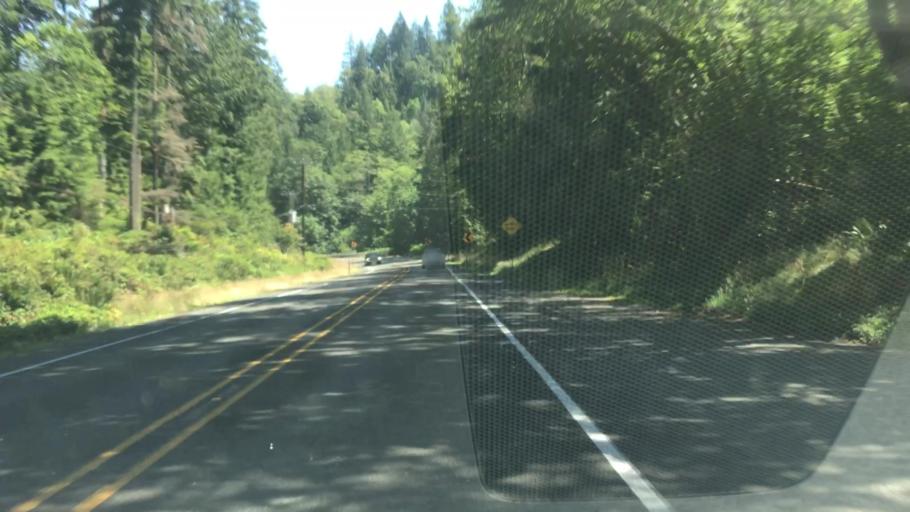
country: US
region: Washington
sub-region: Snohomish County
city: Gold Bar
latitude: 47.8151
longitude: -121.5994
